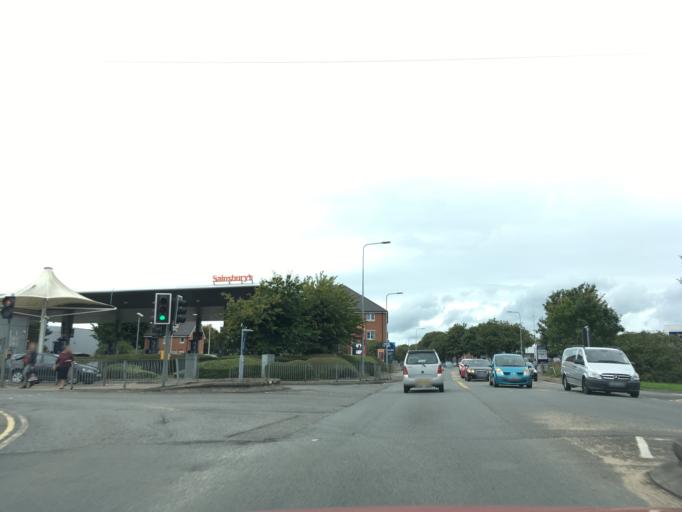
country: GB
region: Wales
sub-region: Cardiff
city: Cardiff
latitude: 51.4960
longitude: -3.1455
